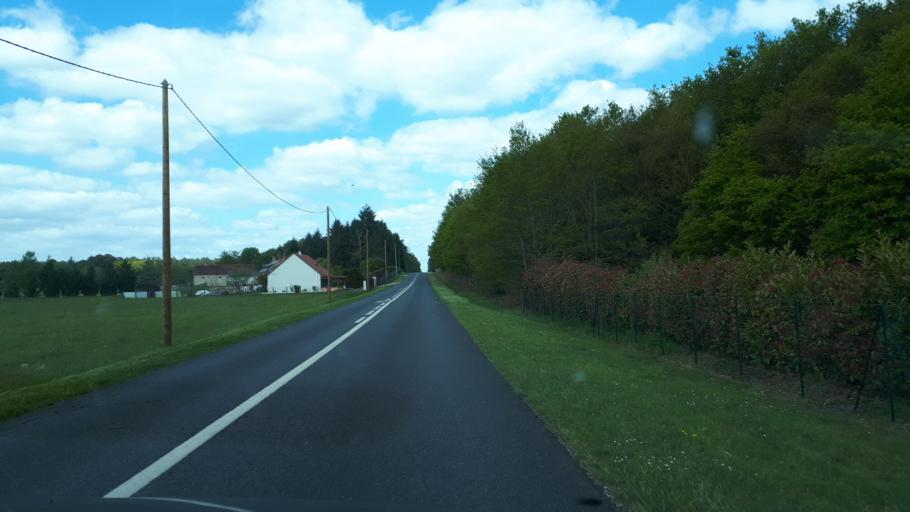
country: FR
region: Centre
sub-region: Departement du Loir-et-Cher
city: Nouan-le-Fuzelier
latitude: 47.5347
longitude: 2.0253
